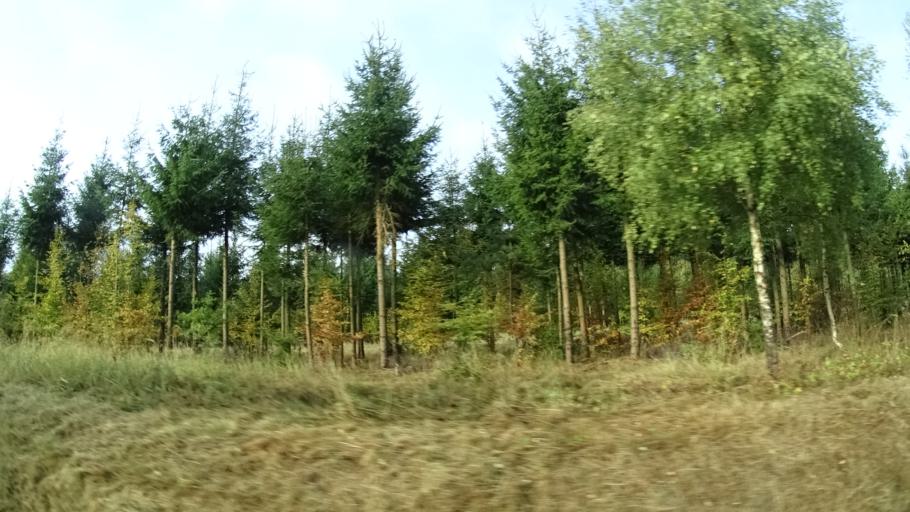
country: DE
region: Hesse
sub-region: Regierungsbezirk Giessen
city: Grebenhain
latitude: 50.4945
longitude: 9.3979
